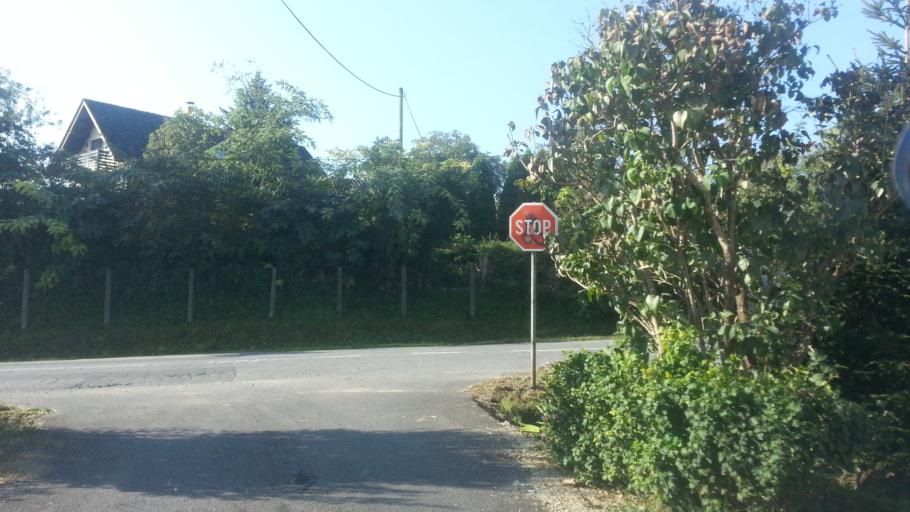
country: RS
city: Stari Banovci
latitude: 44.9826
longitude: 20.2799
